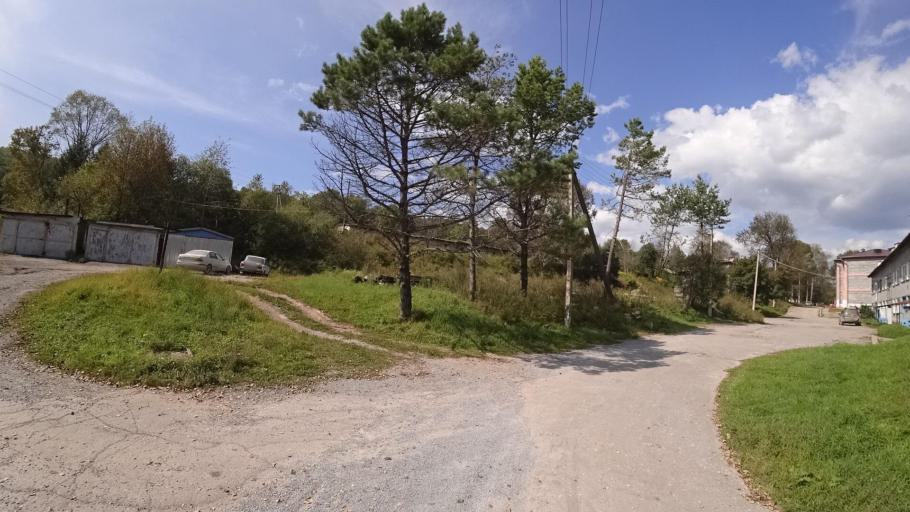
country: RU
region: Jewish Autonomous Oblast
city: Londoko
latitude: 49.0229
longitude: 131.9228
